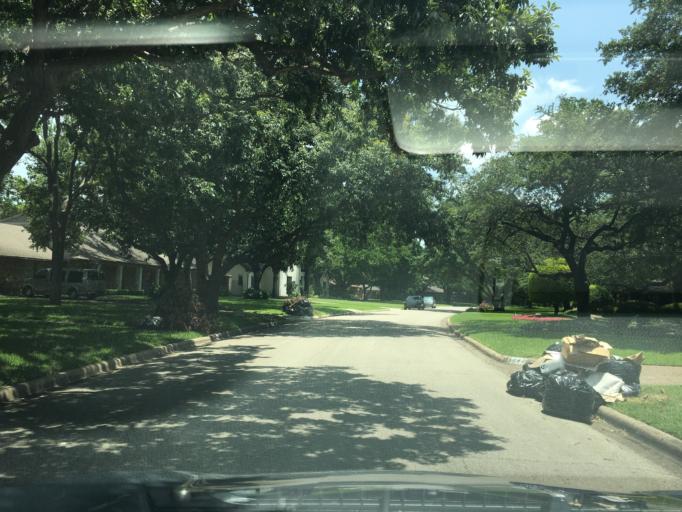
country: US
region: Texas
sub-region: Dallas County
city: Addison
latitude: 32.9117
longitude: -96.8099
